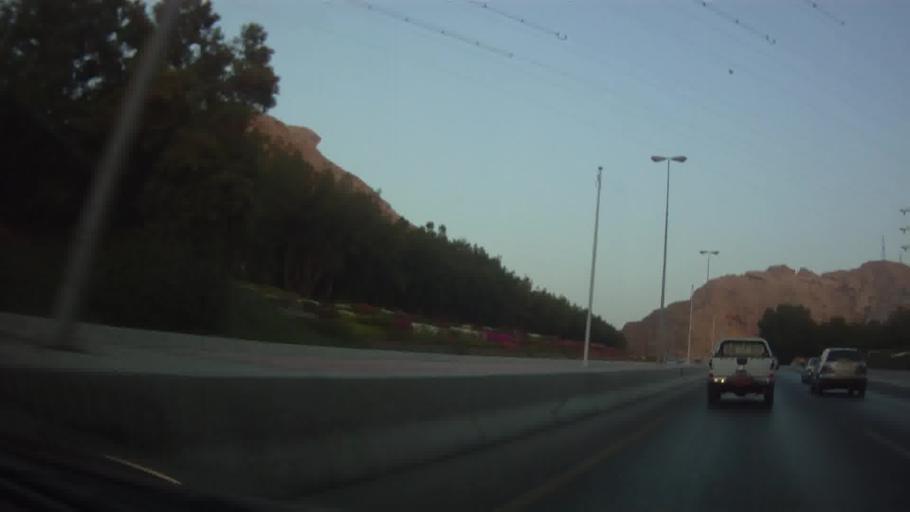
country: OM
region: Muhafazat Masqat
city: Muscat
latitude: 23.6167
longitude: 58.5249
